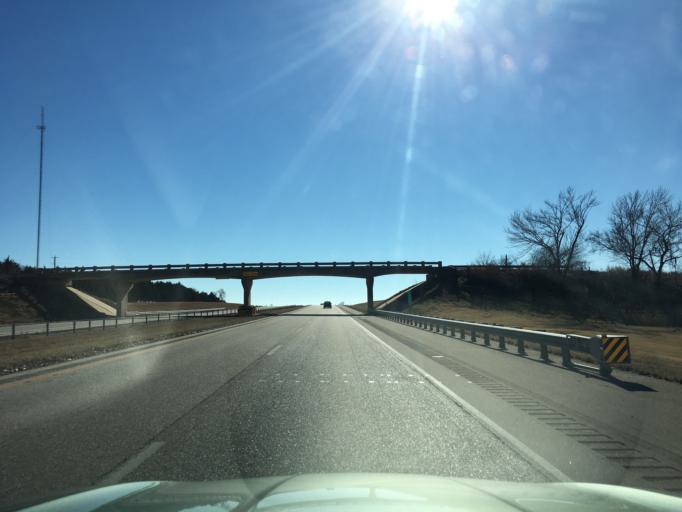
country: US
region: Oklahoma
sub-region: Kay County
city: Blackwell
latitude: 36.8704
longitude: -97.3490
